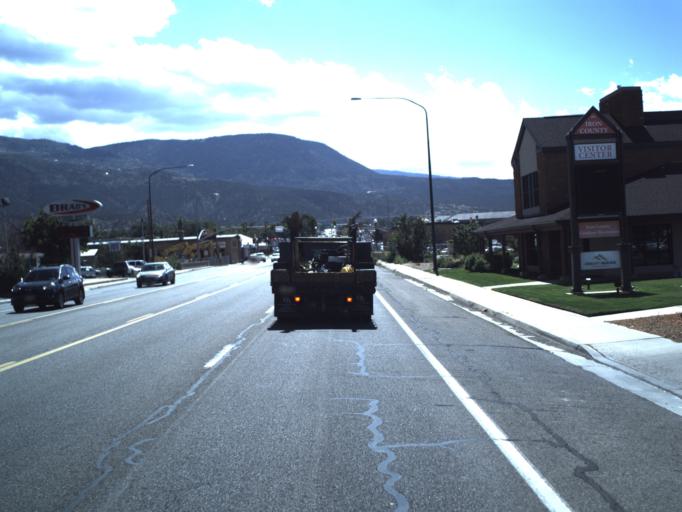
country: US
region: Utah
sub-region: Iron County
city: Cedar City
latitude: 37.6877
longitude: -113.0620
